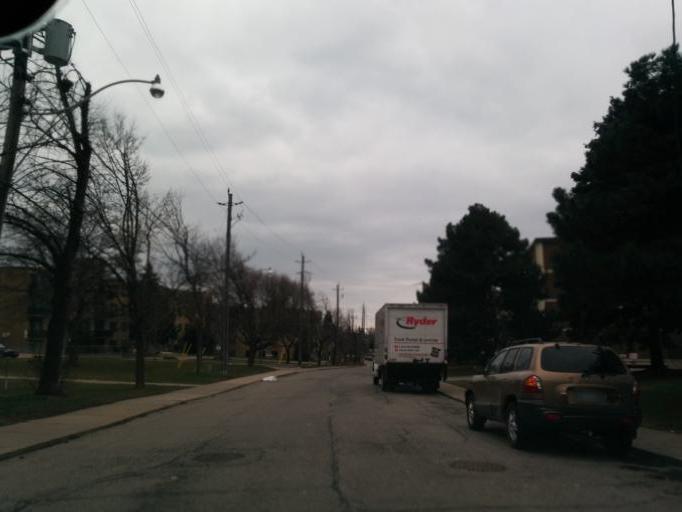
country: CA
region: Ontario
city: Toronto
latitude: 43.6409
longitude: -79.4728
